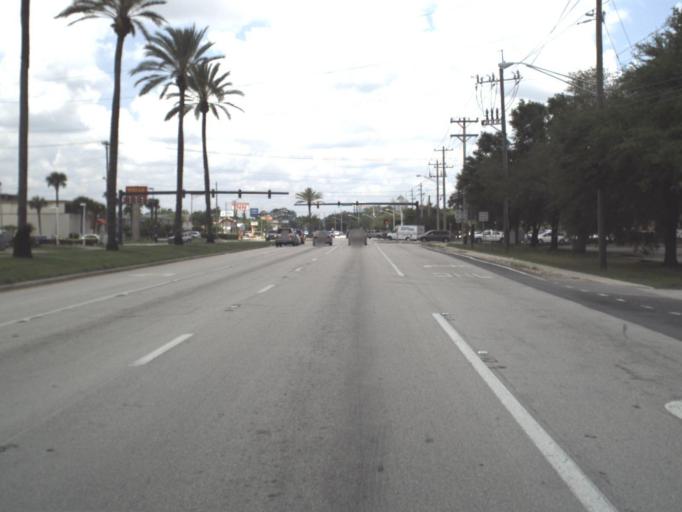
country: US
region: Florida
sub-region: Duval County
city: Jacksonville
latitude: 30.2866
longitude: -81.6327
